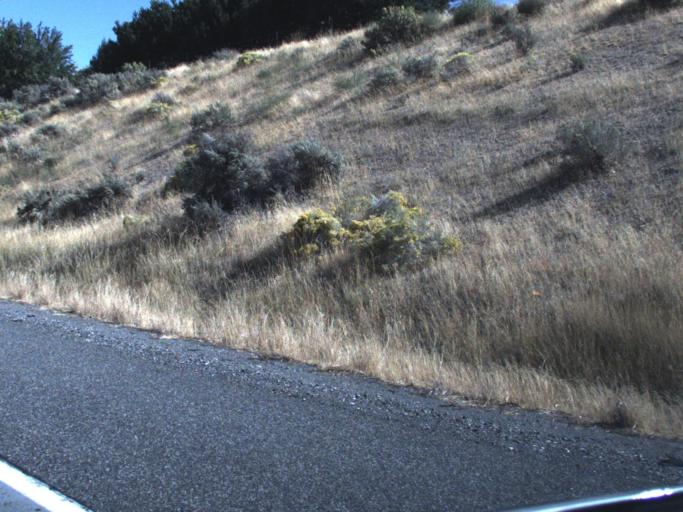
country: US
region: Washington
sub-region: Benton County
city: Richland
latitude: 46.2510
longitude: -119.3147
